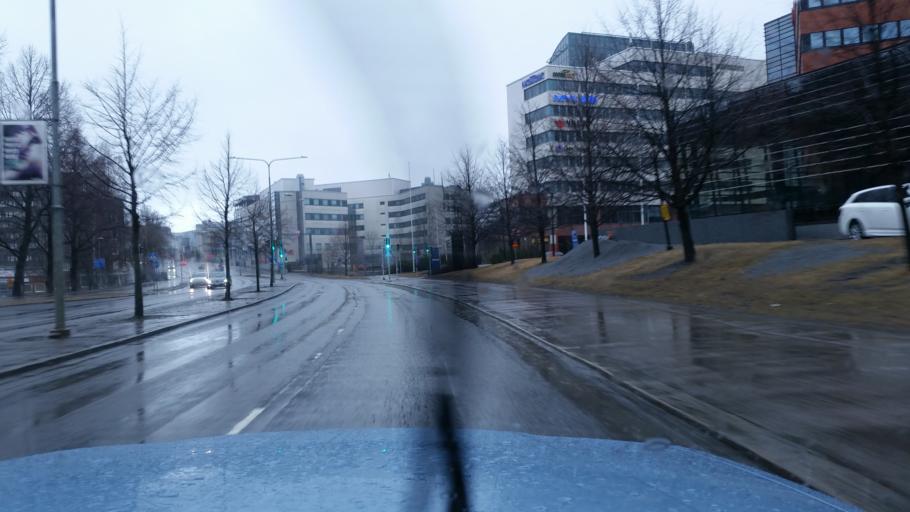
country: FI
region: Pirkanmaa
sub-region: Tampere
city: Tampere
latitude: 61.4890
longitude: 23.7711
